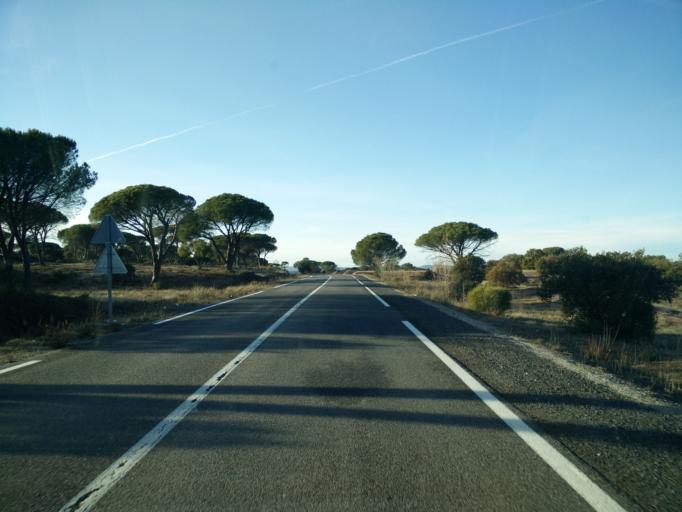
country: FR
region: Provence-Alpes-Cote d'Azur
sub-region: Departement du Var
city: La Garde-Freinet
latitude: 43.3504
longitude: 6.4262
